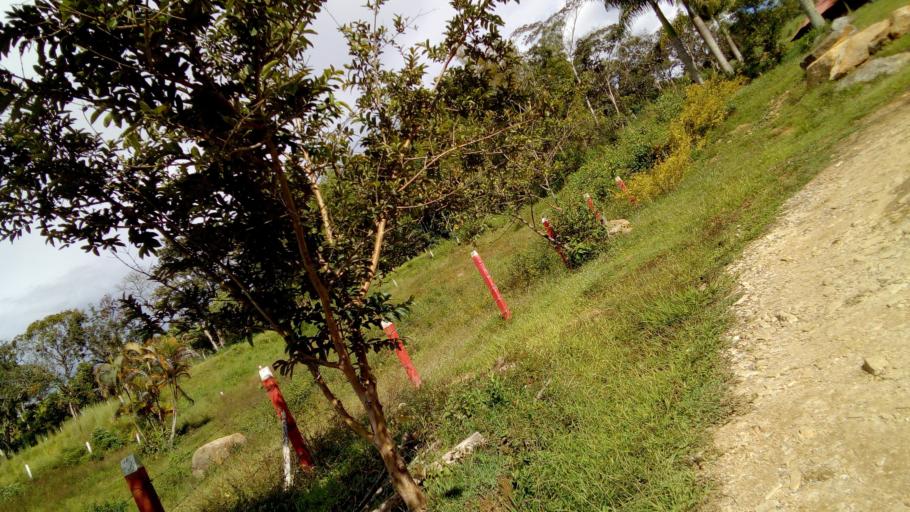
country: CO
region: Boyaca
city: Santana
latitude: 6.0627
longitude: -73.4741
